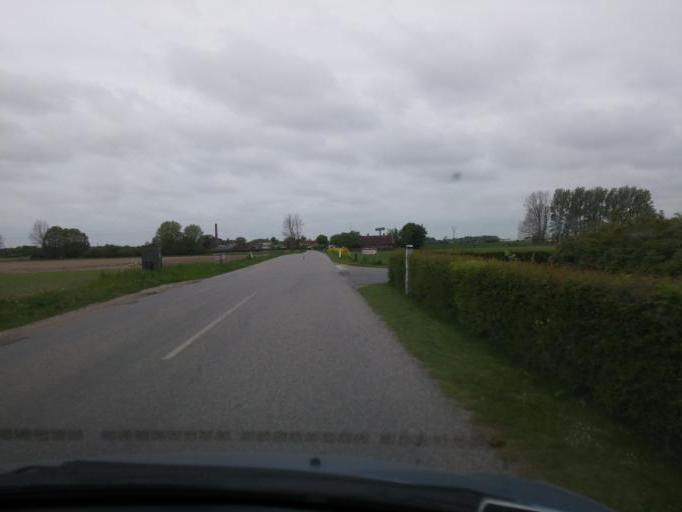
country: DK
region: South Denmark
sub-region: Kerteminde Kommune
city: Munkebo
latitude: 55.4057
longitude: 10.5400
